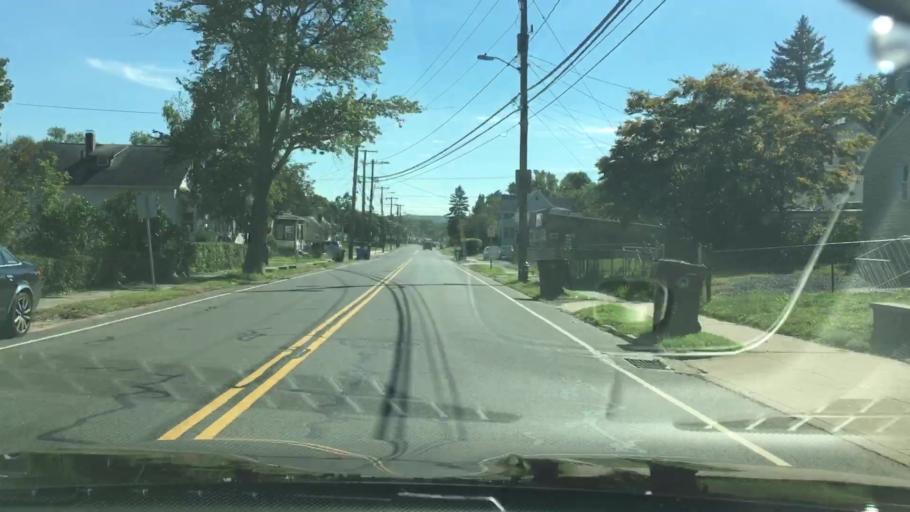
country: US
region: Connecticut
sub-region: Hartford County
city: New Britain
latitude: 41.6579
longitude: -72.7643
